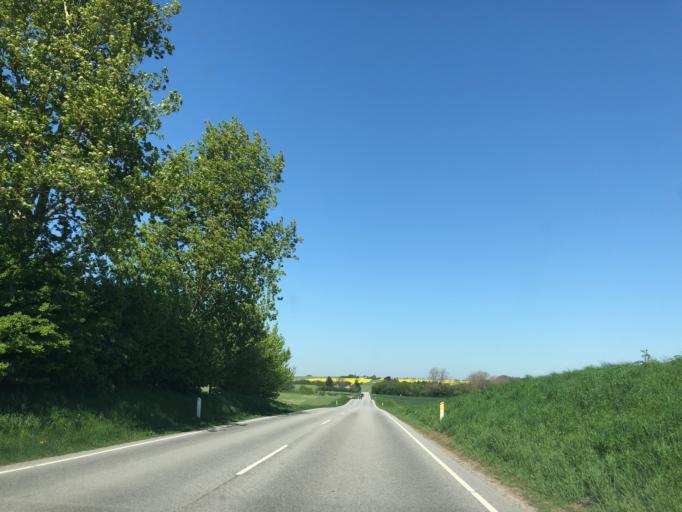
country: DK
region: Zealand
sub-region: Slagelse Kommune
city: Skaelskor
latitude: 55.3129
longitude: 11.2946
